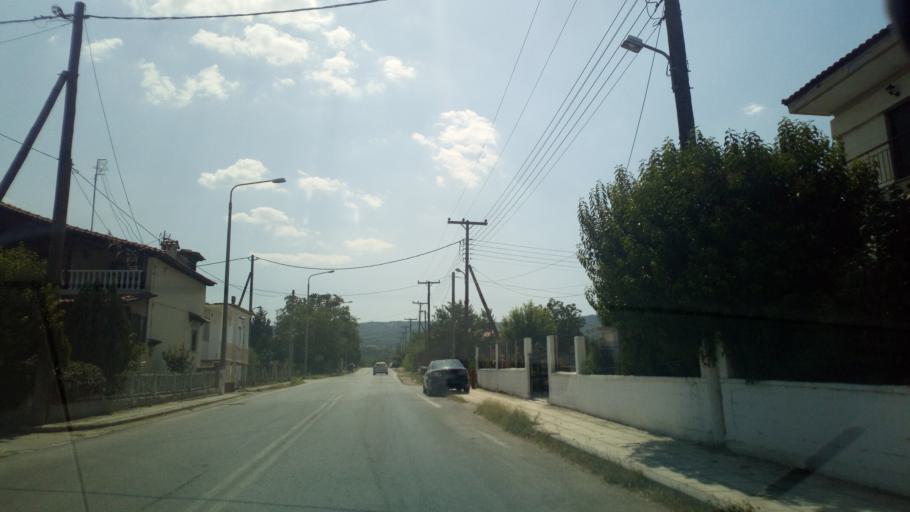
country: GR
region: Central Macedonia
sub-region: Nomos Thessalonikis
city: Agios Vasileios
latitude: 40.6638
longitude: 23.1156
